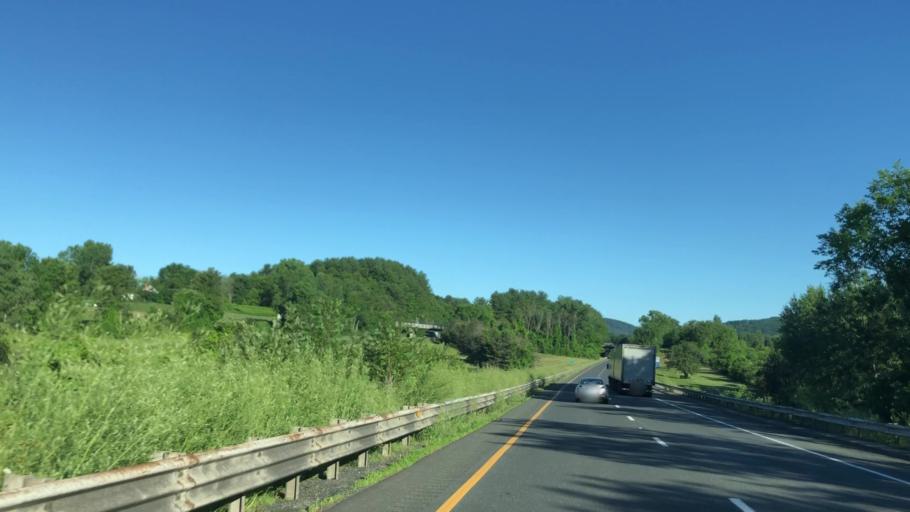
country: US
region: Massachusetts
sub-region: Berkshire County
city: West Stockbridge
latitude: 42.3387
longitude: -73.3855
